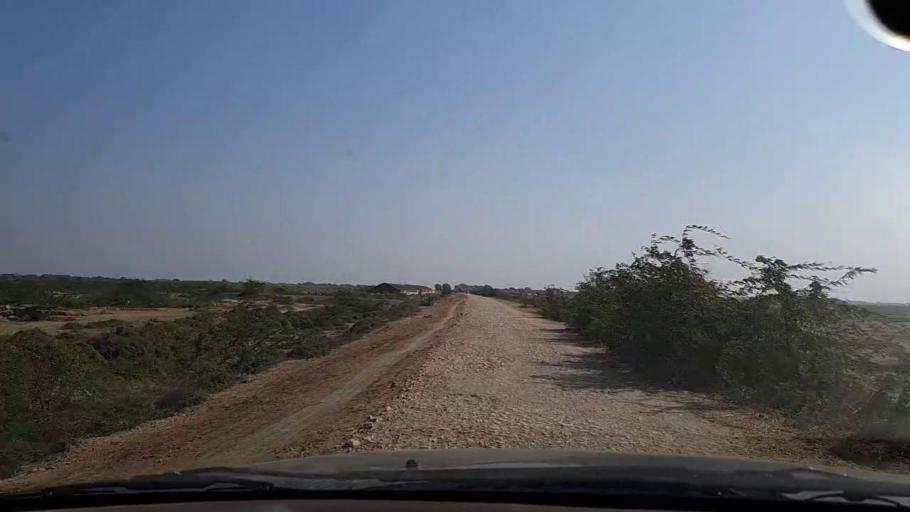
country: PK
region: Sindh
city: Chuhar Jamali
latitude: 24.4210
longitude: 67.8235
